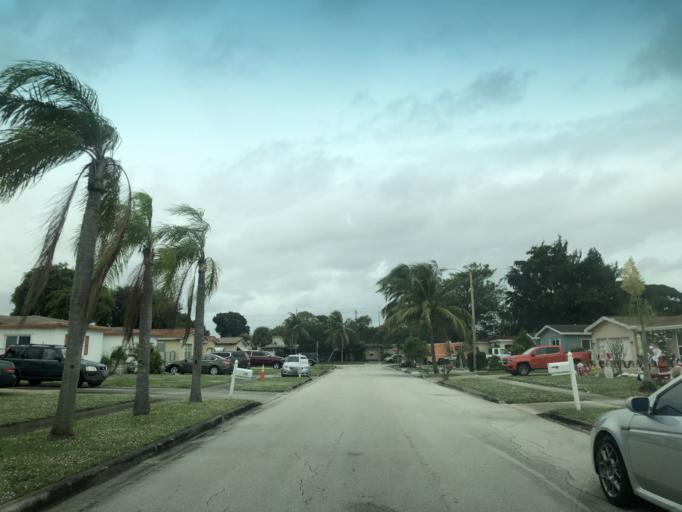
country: US
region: Florida
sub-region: Broward County
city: North Lauderdale
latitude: 26.2340
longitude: -80.2324
